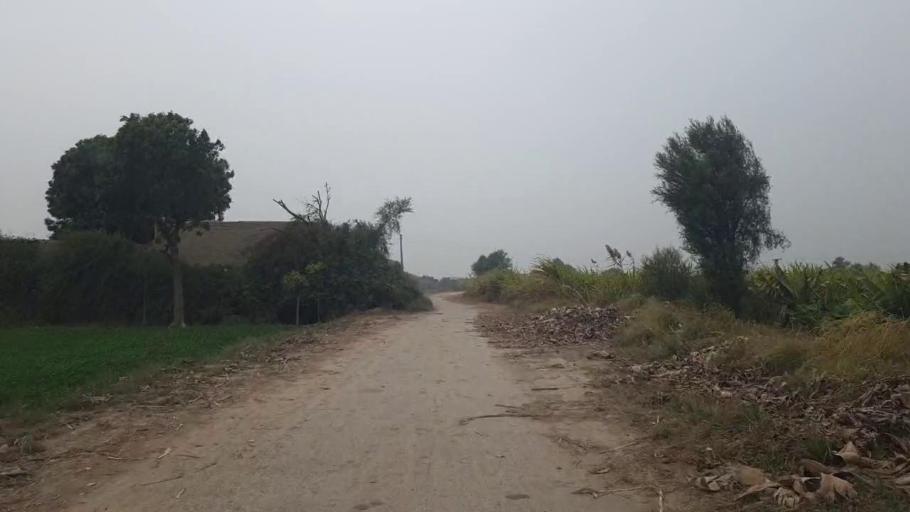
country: PK
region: Sindh
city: Shahdadpur
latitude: 25.8651
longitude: 68.6158
